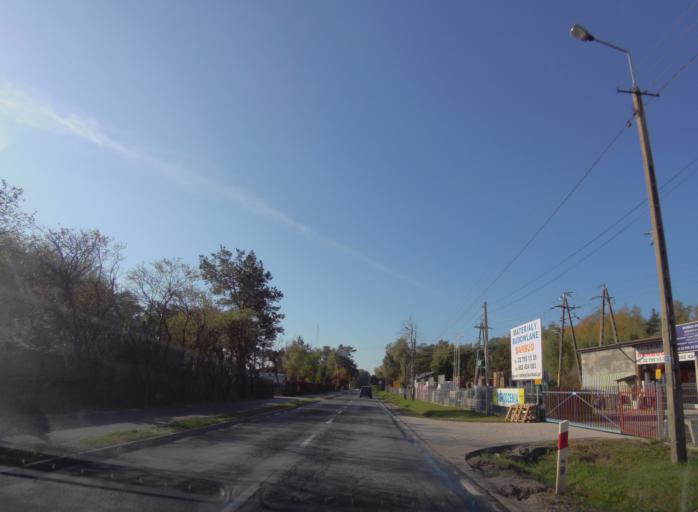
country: PL
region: Masovian Voivodeship
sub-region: Powiat minski
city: Halinow
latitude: 52.2014
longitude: 21.3795
